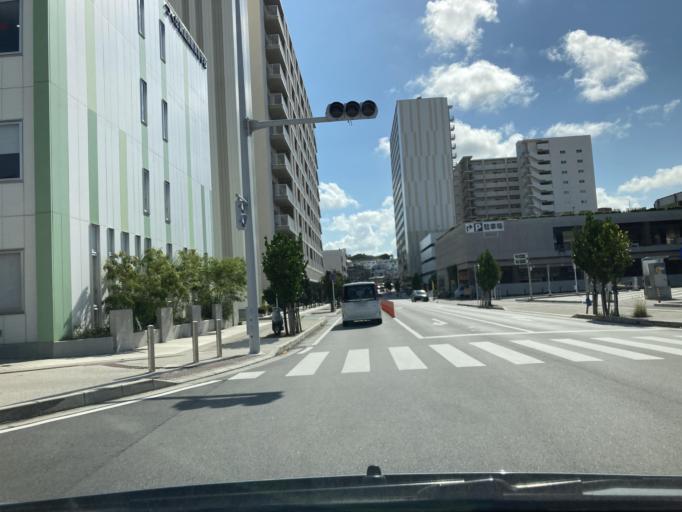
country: JP
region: Okinawa
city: Naha-shi
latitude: 26.2115
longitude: 127.6909
